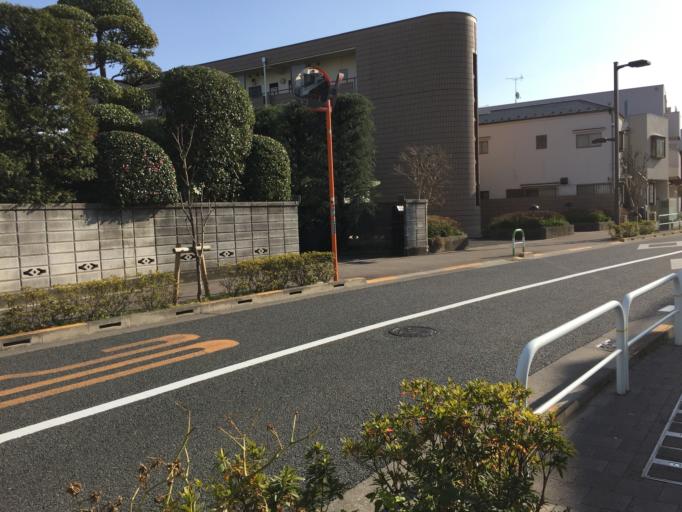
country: JP
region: Tokyo
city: Mitaka-shi
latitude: 35.6690
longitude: 139.6090
